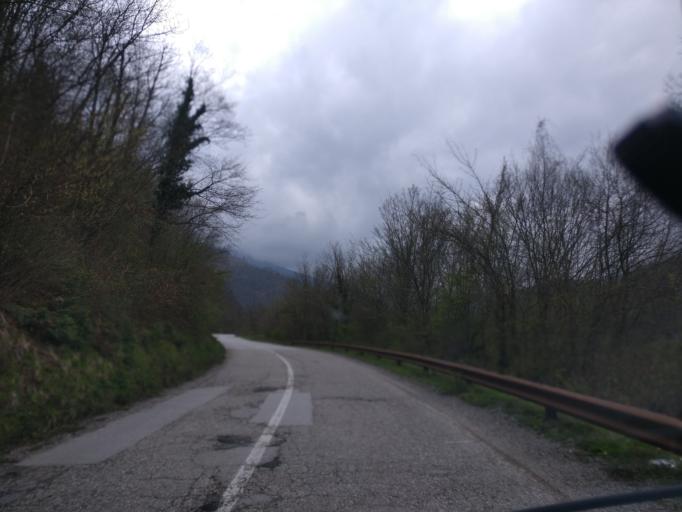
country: BA
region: Republika Srpska
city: Foca
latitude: 43.4578
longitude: 18.7478
